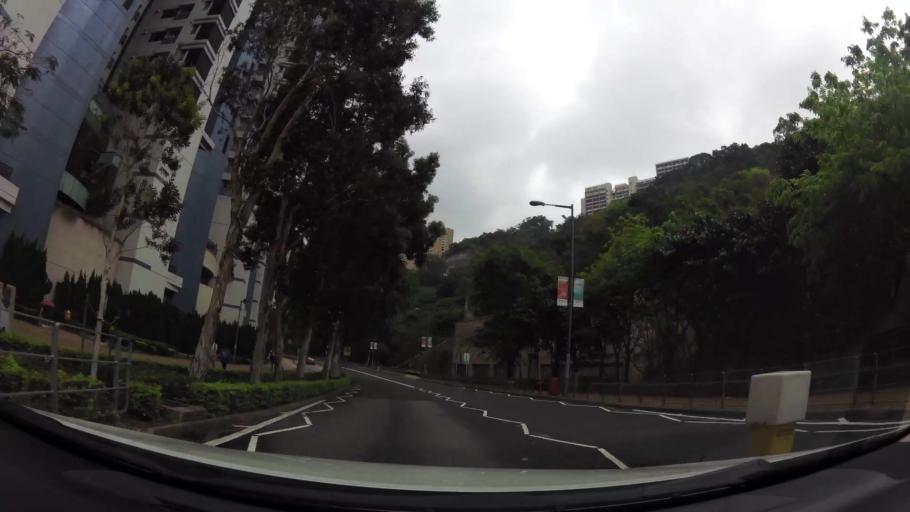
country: HK
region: Central and Western
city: Central
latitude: 22.2572
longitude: 114.1328
